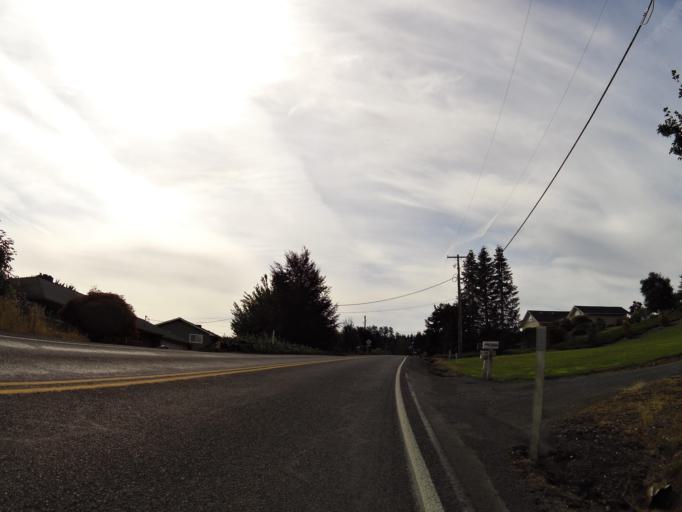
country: US
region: Washington
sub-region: Lewis County
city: Chehalis
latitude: 46.6269
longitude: -122.9673
